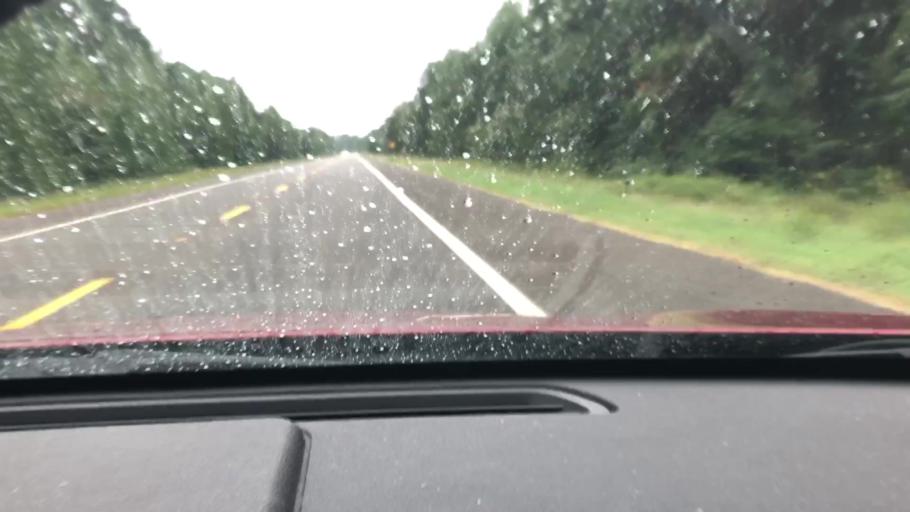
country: US
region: Arkansas
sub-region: Columbia County
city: Waldo
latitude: 33.3054
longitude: -93.2735
